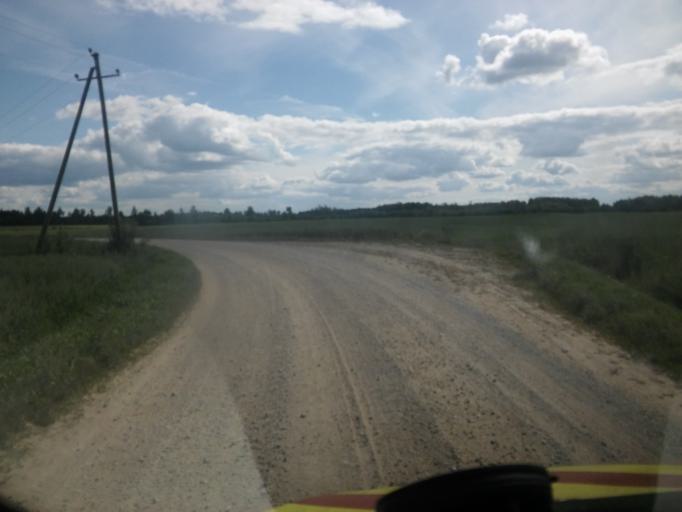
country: EE
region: Viljandimaa
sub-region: Karksi vald
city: Karksi-Nuia
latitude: 58.0709
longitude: 25.5191
